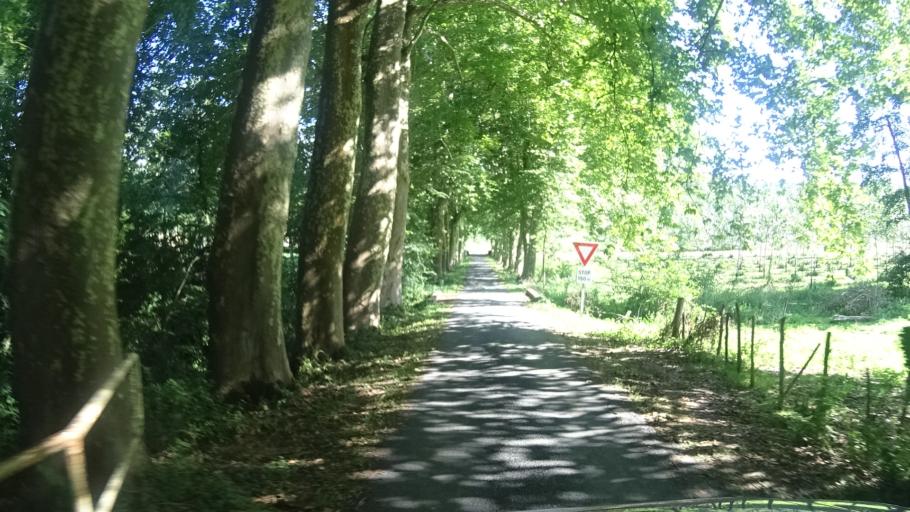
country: FR
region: Aquitaine
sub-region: Departement de la Dordogne
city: Sourzac
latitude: 45.0149
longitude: 0.4385
